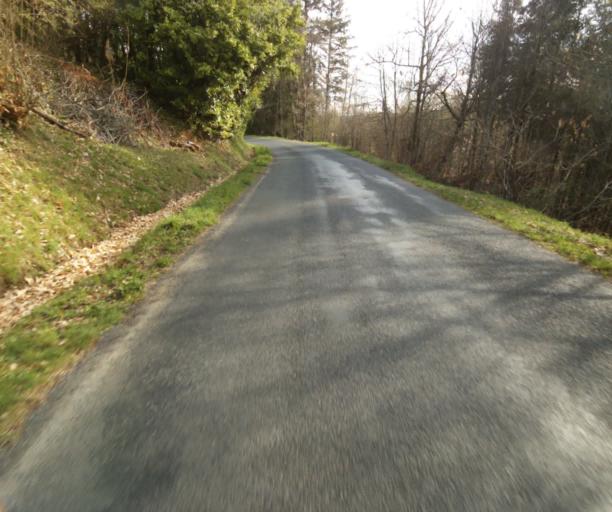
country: FR
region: Limousin
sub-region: Departement de la Correze
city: Correze
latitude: 45.3671
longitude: 1.8688
